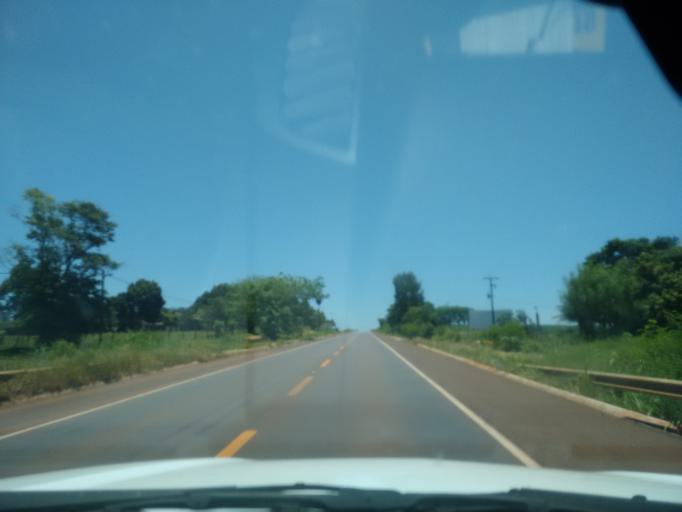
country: PY
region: Canindeyu
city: Salto del Guaira
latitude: -24.1235
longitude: -54.2401
